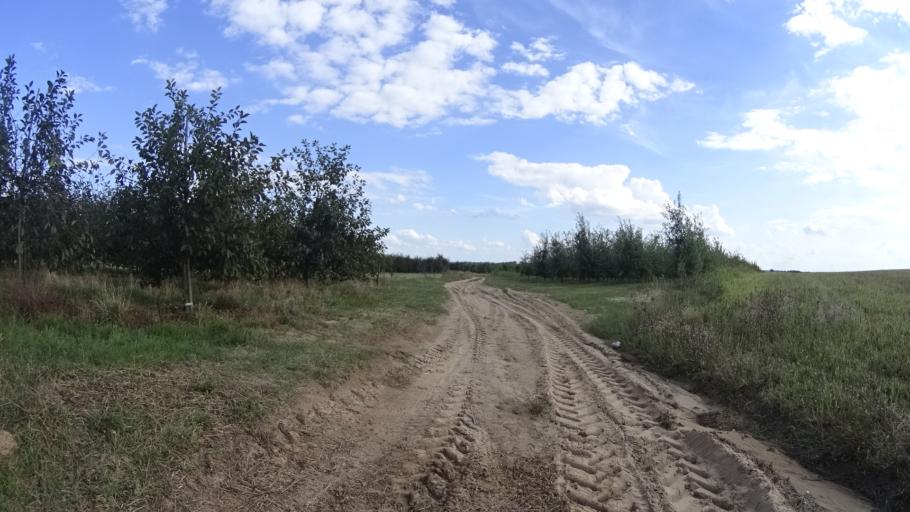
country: PL
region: Masovian Voivodeship
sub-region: Powiat bialobrzeski
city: Wysmierzyce
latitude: 51.6670
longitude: 20.8106
